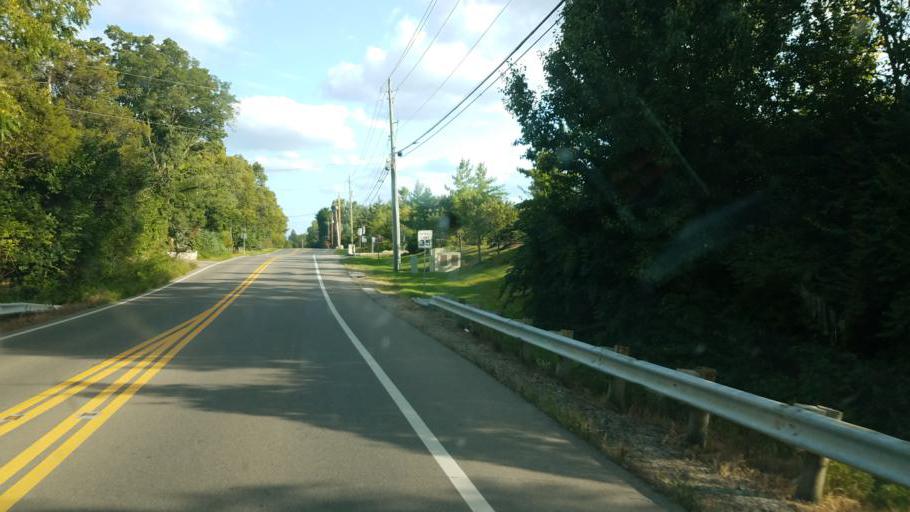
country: US
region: Ohio
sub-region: Franklin County
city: Worthington
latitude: 40.0706
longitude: -83.0423
